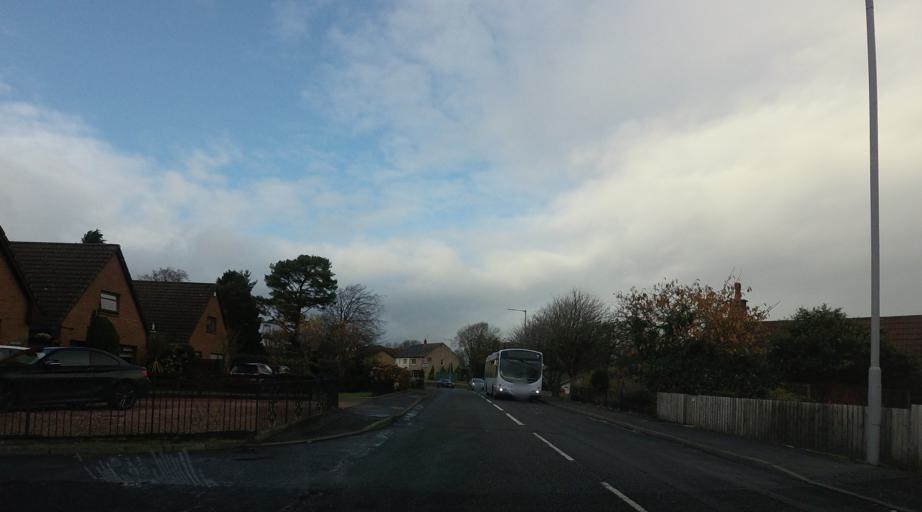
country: GB
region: Scotland
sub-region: Falkirk
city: Polmont
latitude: 55.9770
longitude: -3.7125
